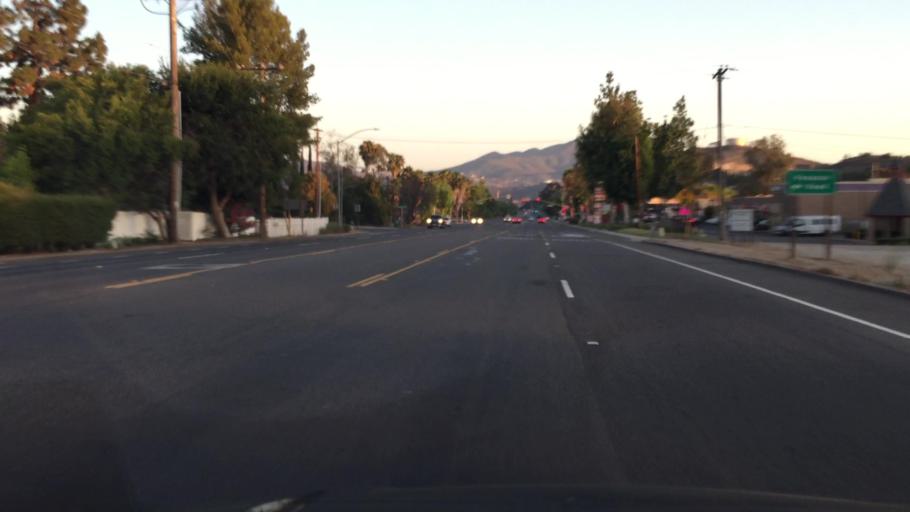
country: US
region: California
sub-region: San Diego County
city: Rancho San Diego
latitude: 32.7712
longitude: -116.9279
